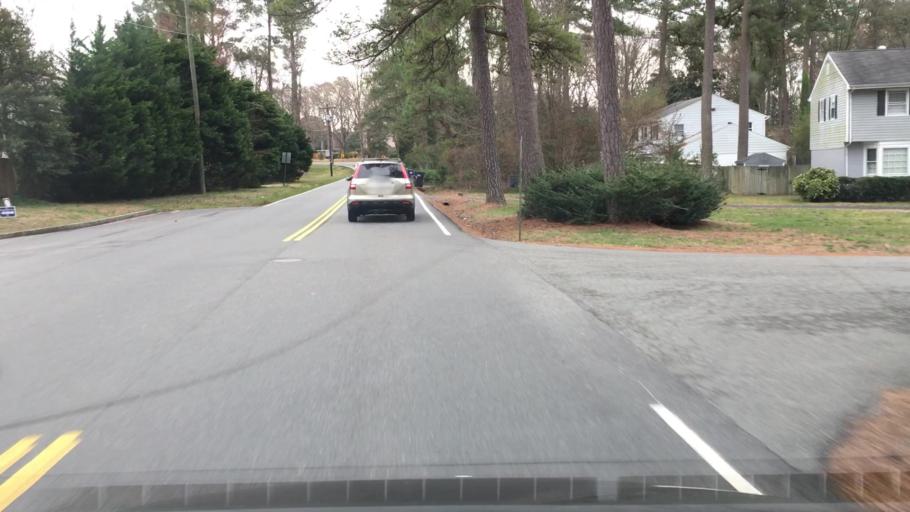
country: US
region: Virginia
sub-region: Henrico County
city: Tuckahoe
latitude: 37.5894
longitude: -77.5926
